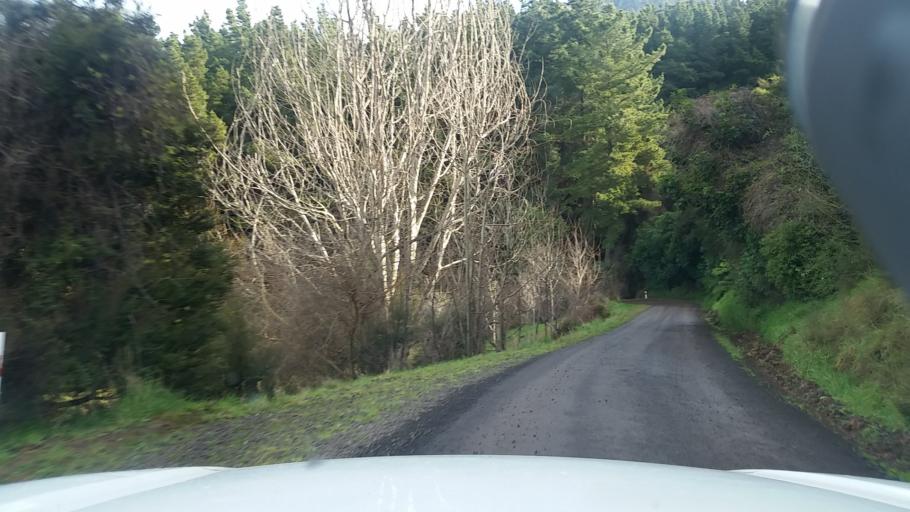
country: NZ
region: Canterbury
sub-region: Christchurch City
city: Christchurch
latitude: -43.6729
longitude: 172.8756
